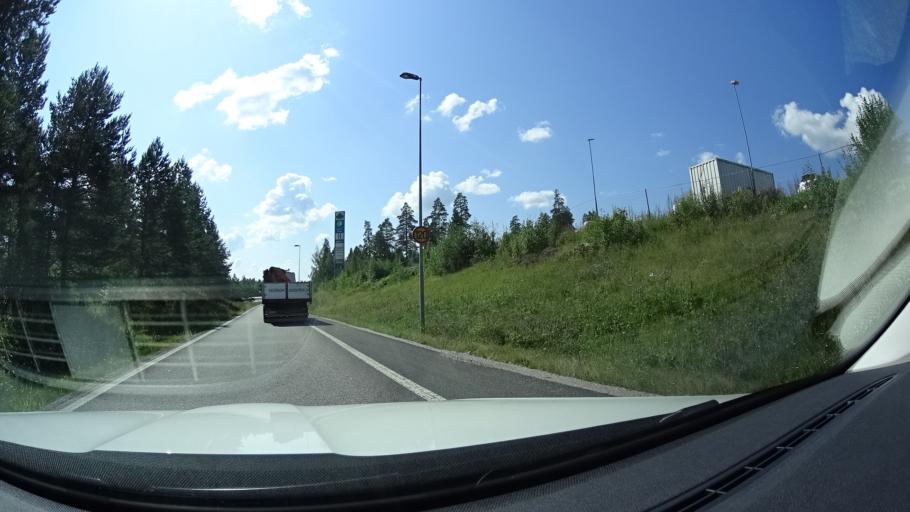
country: FI
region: Uusimaa
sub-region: Helsinki
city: Nurmijaervi
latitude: 60.4548
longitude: 24.8442
